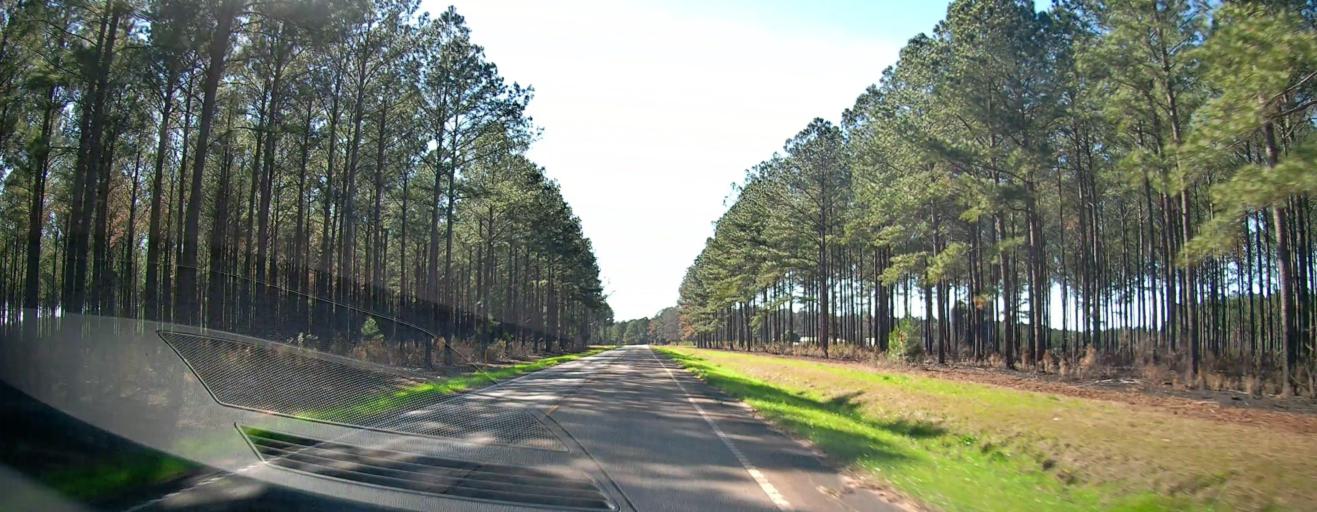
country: US
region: Georgia
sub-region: Schley County
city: Ellaville
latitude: 32.1910
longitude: -84.2283
